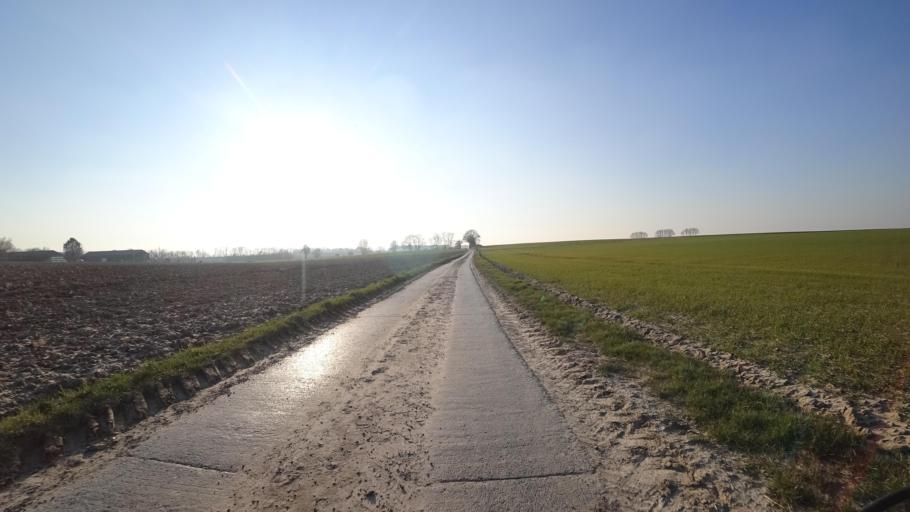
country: BE
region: Wallonia
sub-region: Province du Brabant Wallon
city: Chaumont-Gistoux
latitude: 50.6548
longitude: 4.7161
